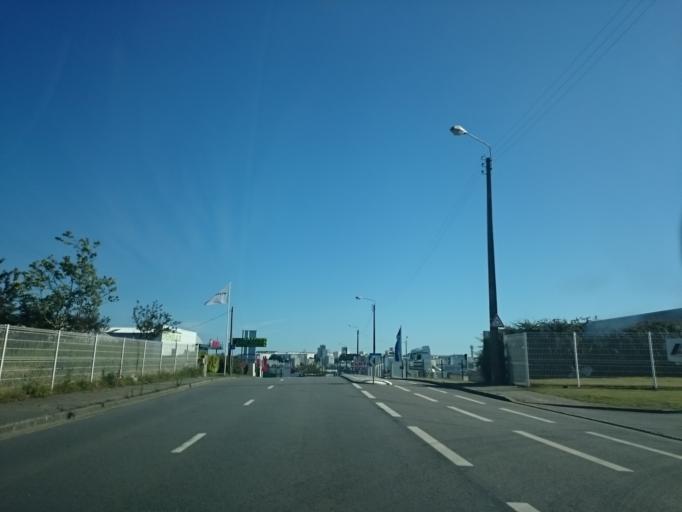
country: FR
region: Brittany
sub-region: Departement du Finistere
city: Brest
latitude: 48.4196
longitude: -4.4632
